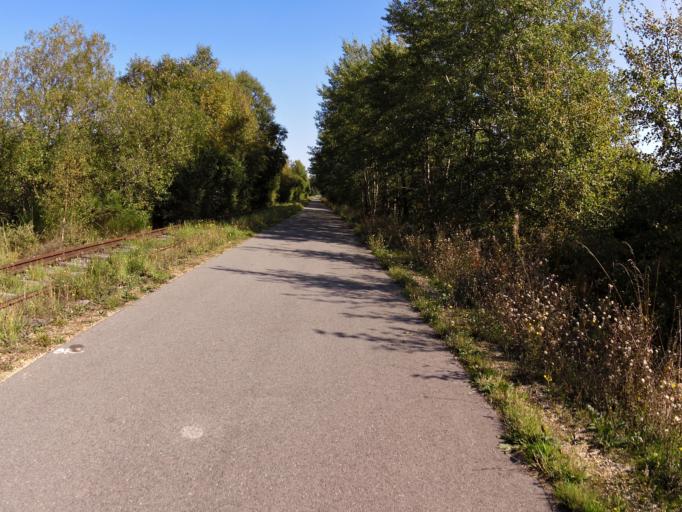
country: BE
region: Wallonia
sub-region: Province de Liege
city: Waimes
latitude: 50.4789
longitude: 6.1502
